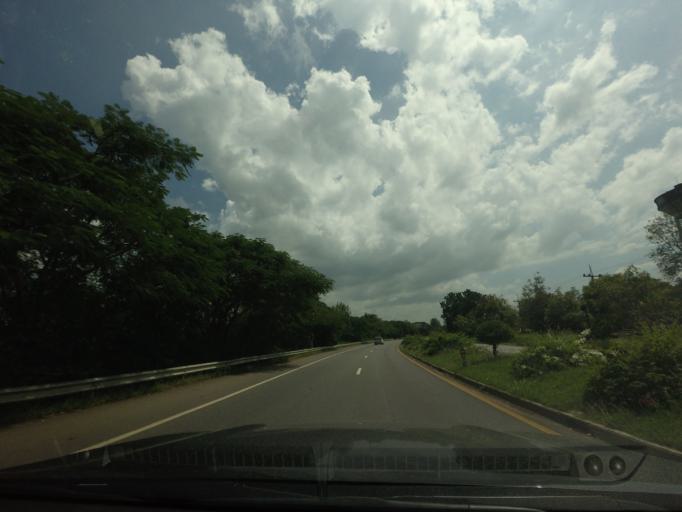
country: TH
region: Phetchabun
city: Phetchabun
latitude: 16.2259
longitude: 101.0886
